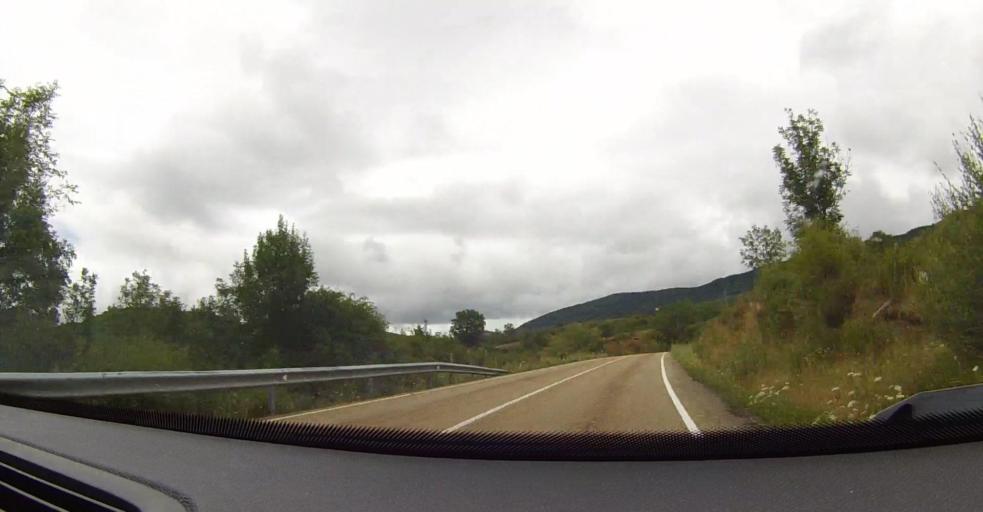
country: ES
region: Castille and Leon
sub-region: Provincia de Leon
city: Reyero
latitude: 42.9437
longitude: -5.2507
